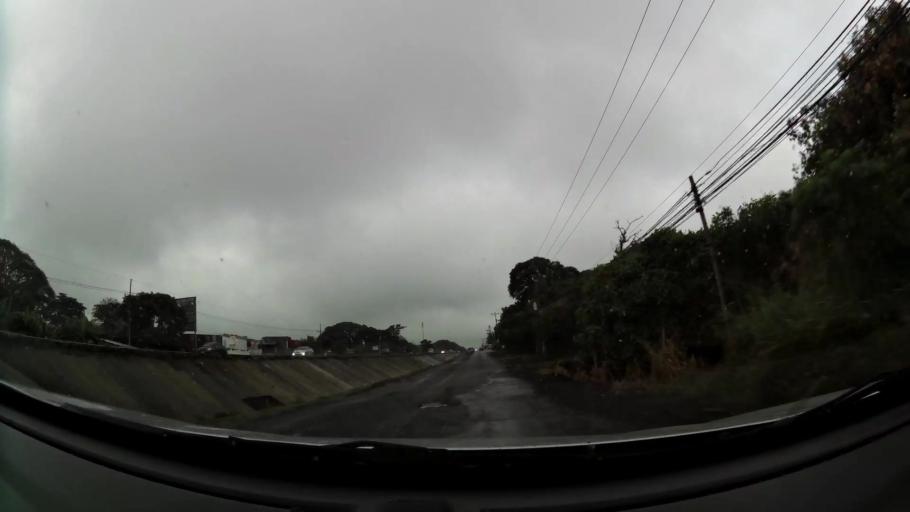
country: CR
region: Alajuela
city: Carrillos
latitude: 9.9963
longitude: -84.2674
